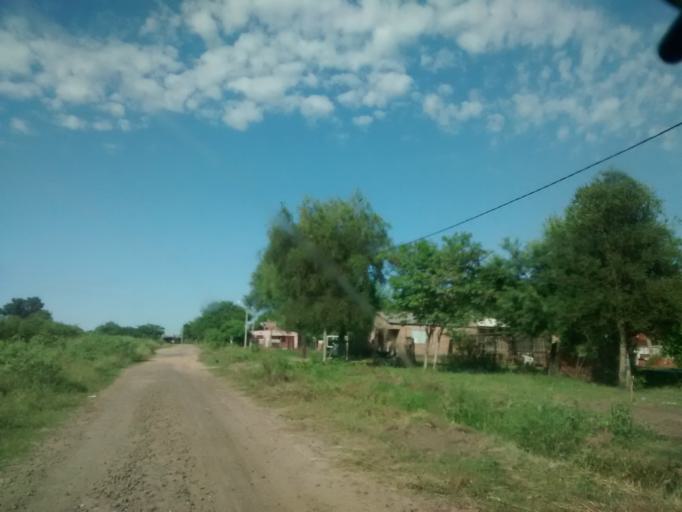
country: AR
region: Chaco
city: Puerto Tirol
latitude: -27.3781
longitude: -59.0939
